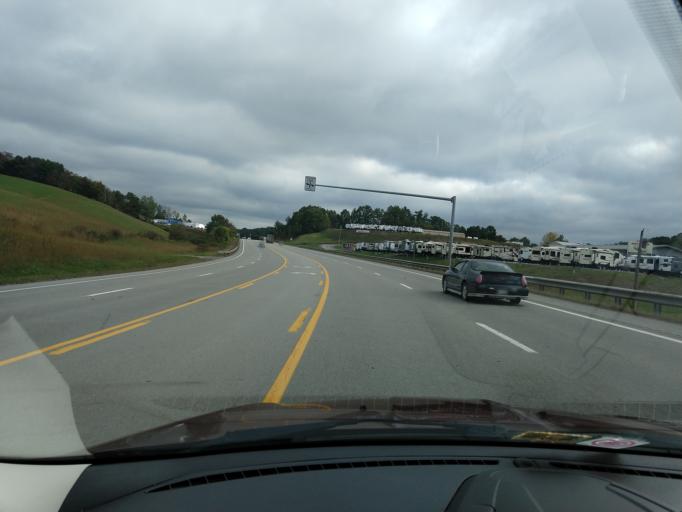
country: US
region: West Virginia
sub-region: Randolph County
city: Elkins
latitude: 38.8743
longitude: -79.8415
